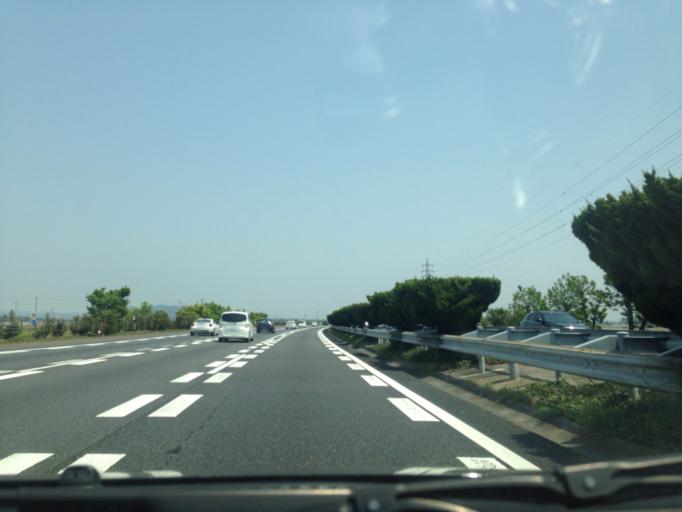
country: JP
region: Gunma
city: Tatebayashi
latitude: 36.2468
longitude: 139.5811
